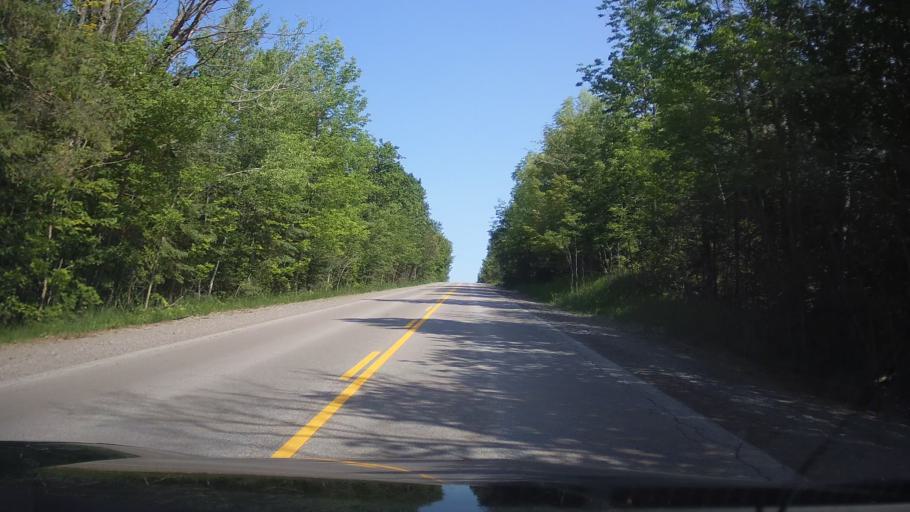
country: CA
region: Ontario
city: Uxbridge
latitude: 44.5047
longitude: -78.9528
